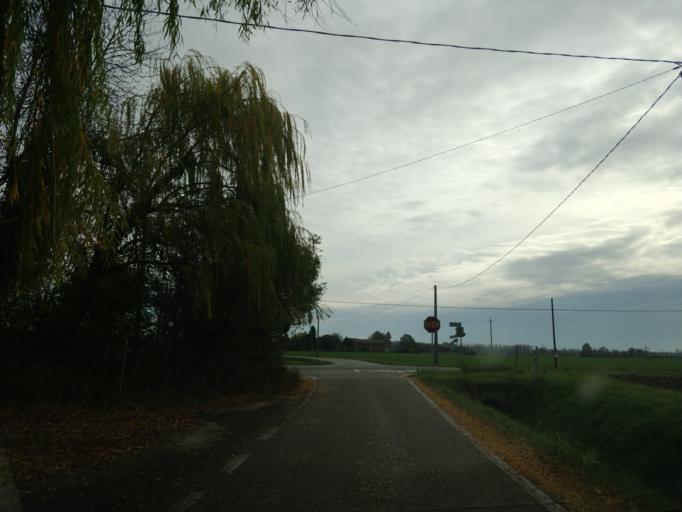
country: IT
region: Emilia-Romagna
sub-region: Provincia di Bologna
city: Argelato
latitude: 44.6133
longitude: 11.3354
